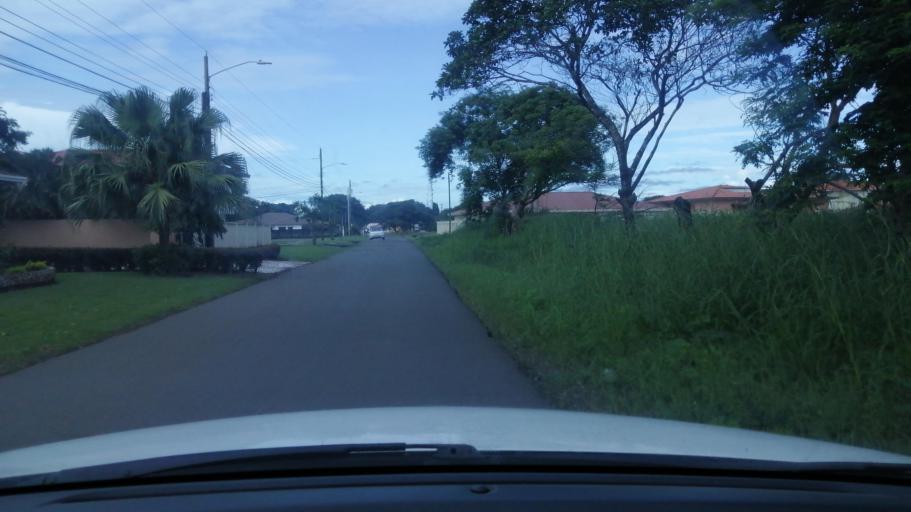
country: PA
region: Chiriqui
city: El Quiteno
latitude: 8.4614
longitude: -82.4172
